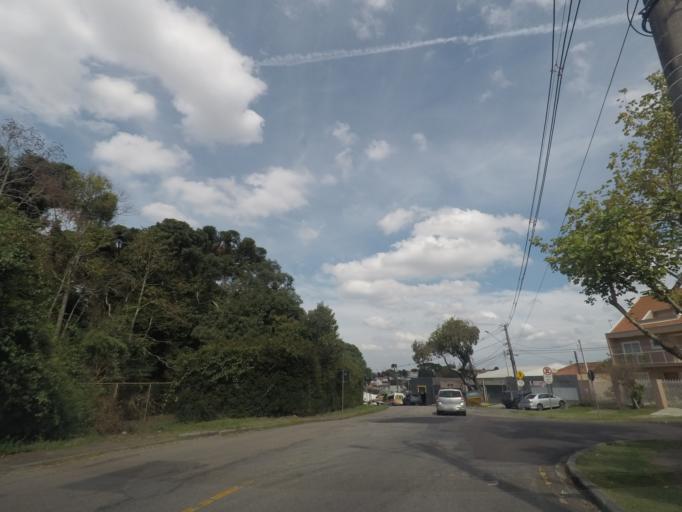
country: BR
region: Parana
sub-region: Curitiba
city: Curitiba
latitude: -25.4894
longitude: -49.2631
